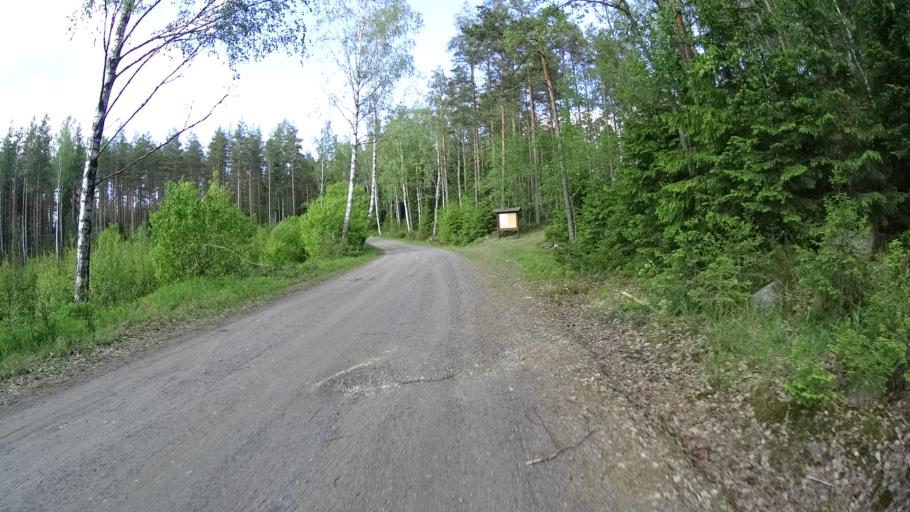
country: FI
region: Uusimaa
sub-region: Raaseporin
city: Pohja
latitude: 60.1389
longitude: 23.5307
